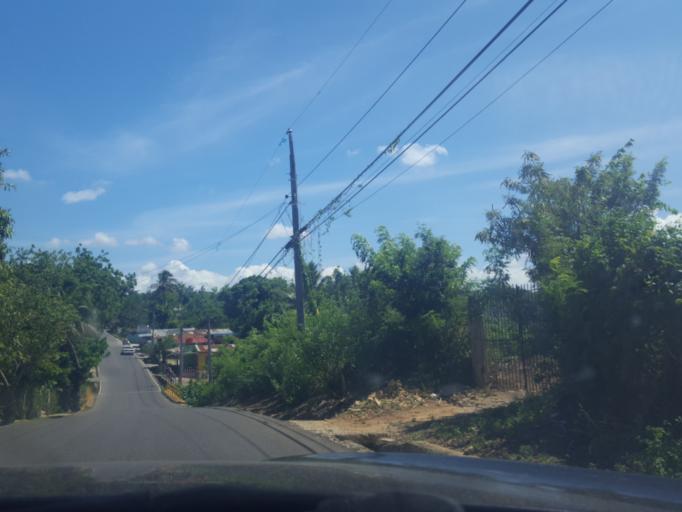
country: DO
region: Santiago
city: Licey al Medio
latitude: 19.3873
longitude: -70.6498
